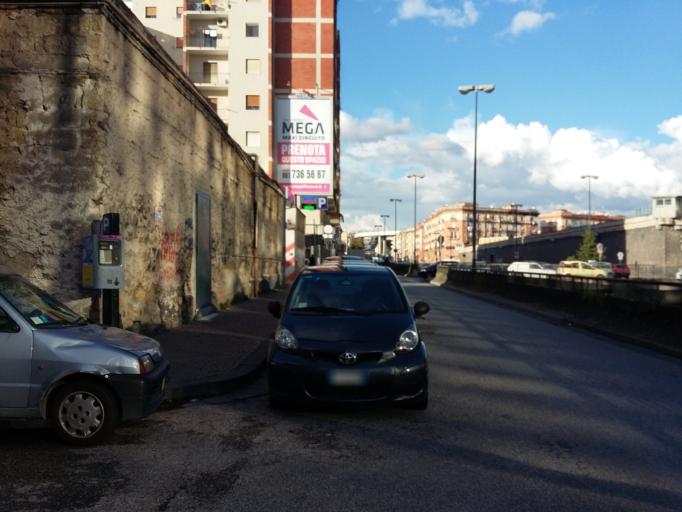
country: IT
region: Campania
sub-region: Provincia di Napoli
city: Napoli
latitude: 40.8577
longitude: 14.2766
